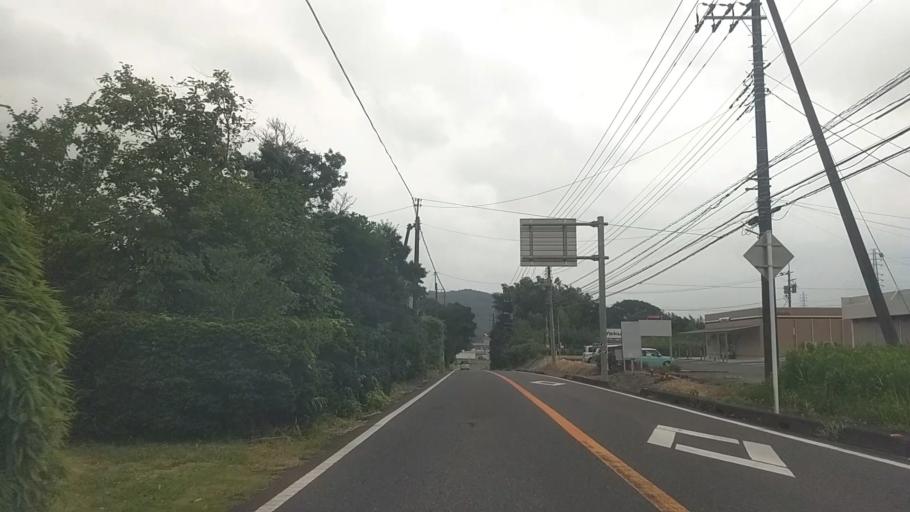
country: JP
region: Chiba
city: Kisarazu
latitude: 35.3117
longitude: 140.0630
